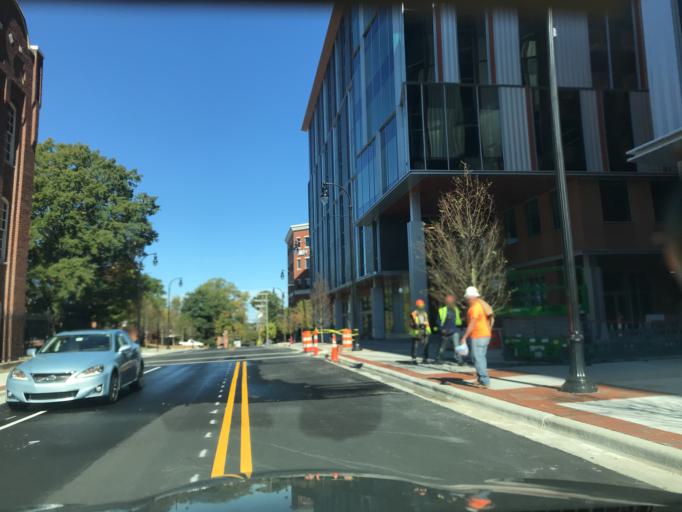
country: US
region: North Carolina
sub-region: Durham County
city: Durham
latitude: 35.9993
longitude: -78.9037
